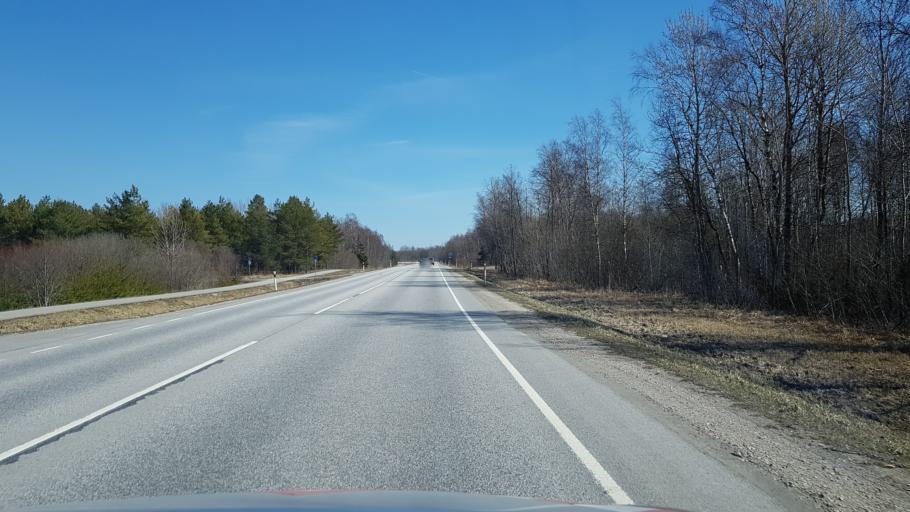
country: EE
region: Laeaene
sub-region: Ridala Parish
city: Uuemoisa
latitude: 58.9490
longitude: 23.6423
